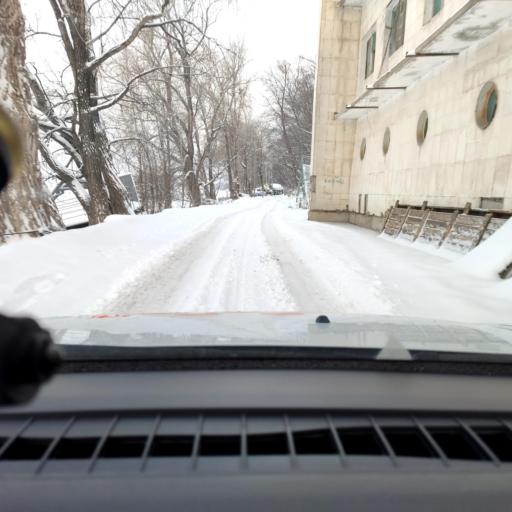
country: RU
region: Samara
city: Samara
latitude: 53.2917
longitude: 50.1921
